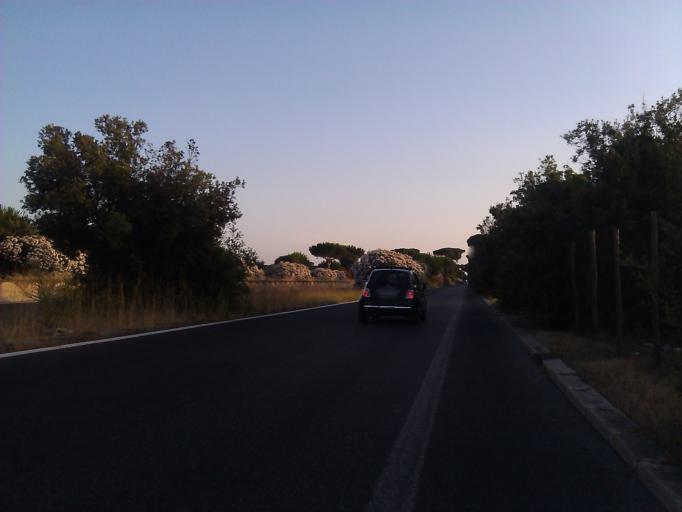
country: IT
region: Latium
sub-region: Citta metropolitana di Roma Capitale
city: Acilia-Castel Fusano-Ostia Antica
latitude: 41.7283
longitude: 12.3348
